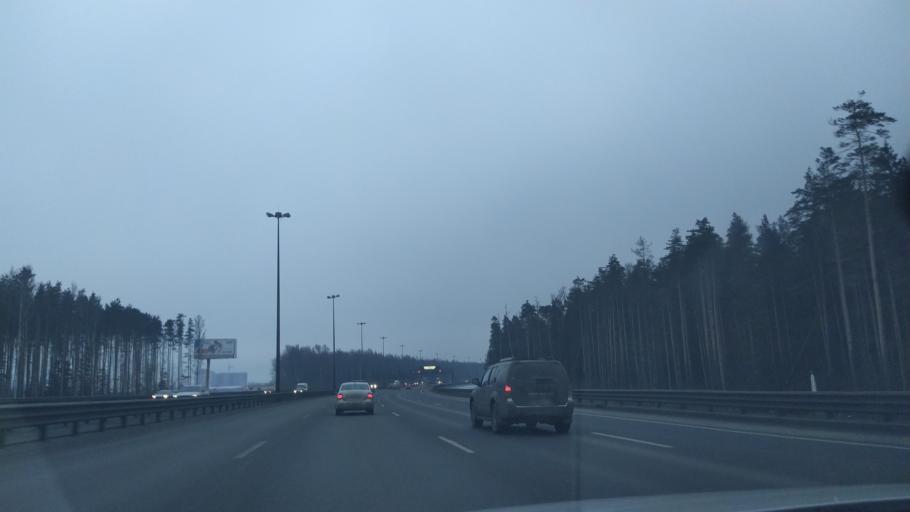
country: RU
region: Leningrad
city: Yanino Vtoroye
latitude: 59.9613
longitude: 30.5537
